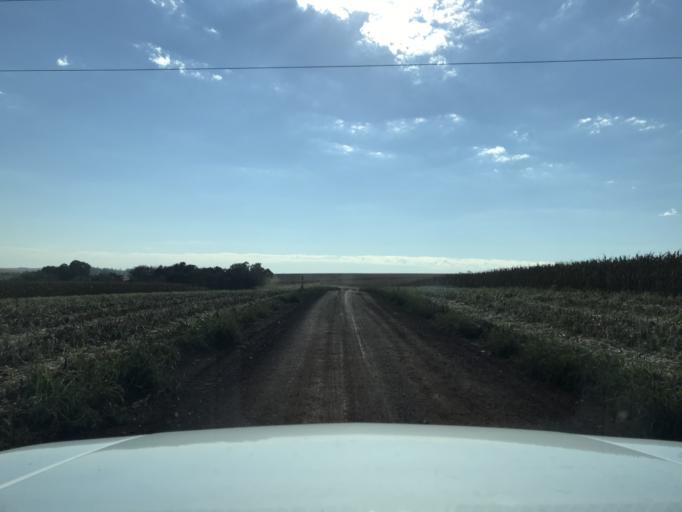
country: BR
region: Parana
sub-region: Palotina
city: Palotina
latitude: -24.2725
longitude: -53.8174
